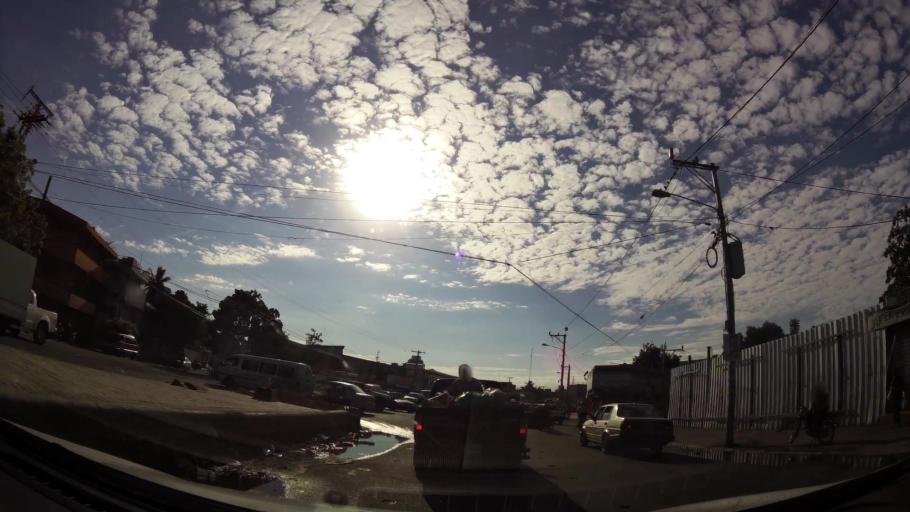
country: DO
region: Santo Domingo
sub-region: Santo Domingo
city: Santo Domingo Este
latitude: 18.5096
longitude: -69.8622
